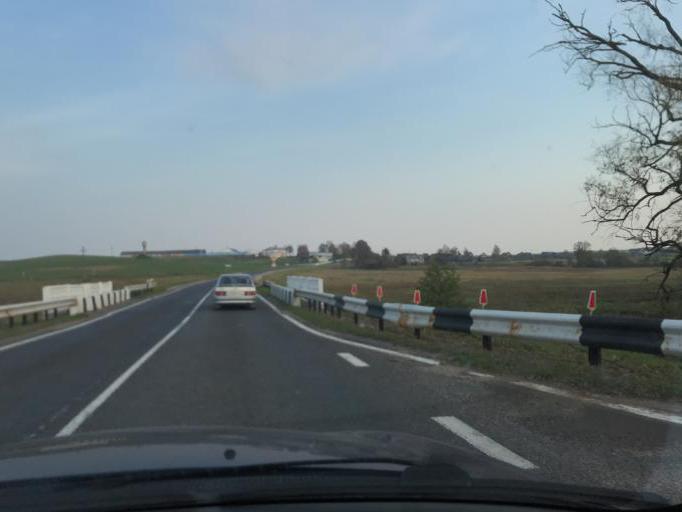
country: BY
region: Grodnenskaya
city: Karelichy
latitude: 53.5893
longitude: 26.0998
